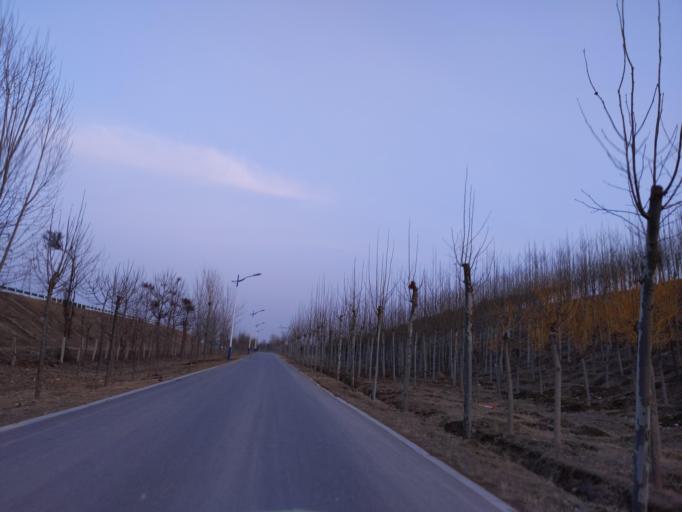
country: CN
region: Henan Sheng
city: Zhongyuanlu
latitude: 35.8146
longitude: 115.0629
